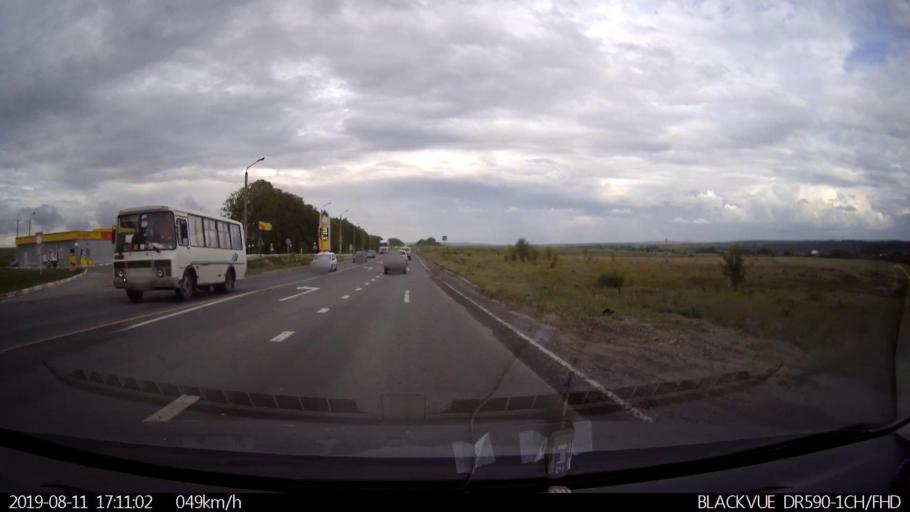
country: RU
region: Ulyanovsk
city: Mayna
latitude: 54.3003
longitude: 47.8811
